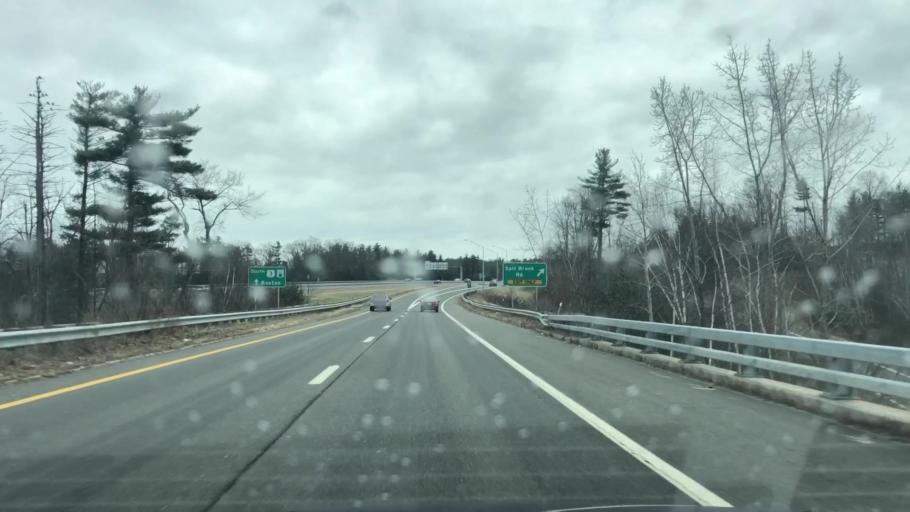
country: US
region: Massachusetts
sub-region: Middlesex County
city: Tyngsboro
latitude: 42.7169
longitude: -71.4511
